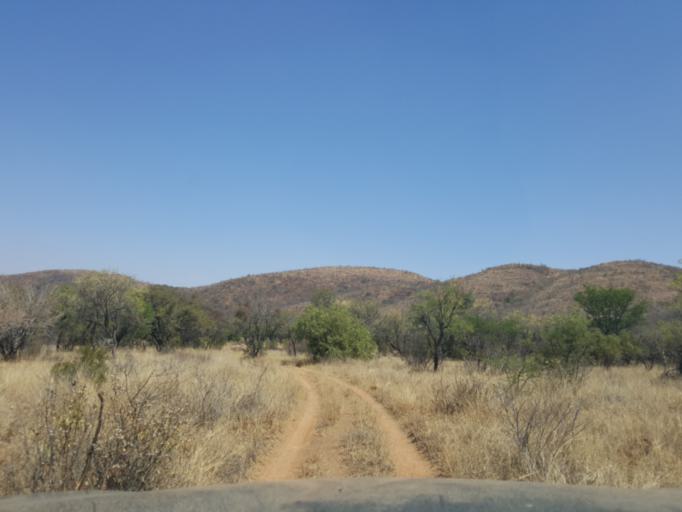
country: BW
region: South East
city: Lobatse
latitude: -25.1405
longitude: 25.6709
